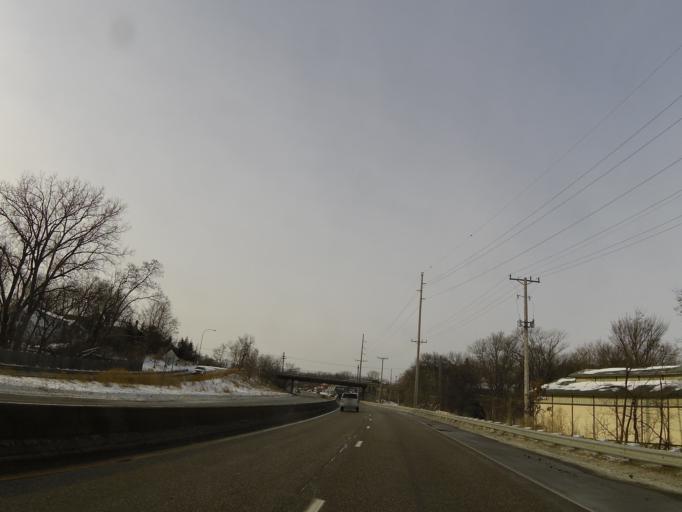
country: US
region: Minnesota
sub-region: Hennepin County
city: Excelsior
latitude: 44.9008
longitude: -93.5600
